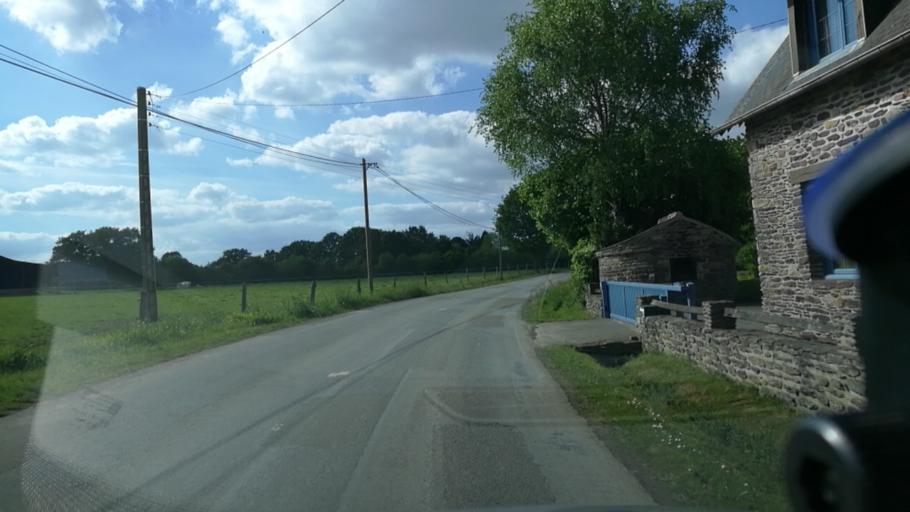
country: FR
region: Brittany
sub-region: Departement d'Ille-et-Vilaine
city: Retiers
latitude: 47.8975
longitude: -1.3540
